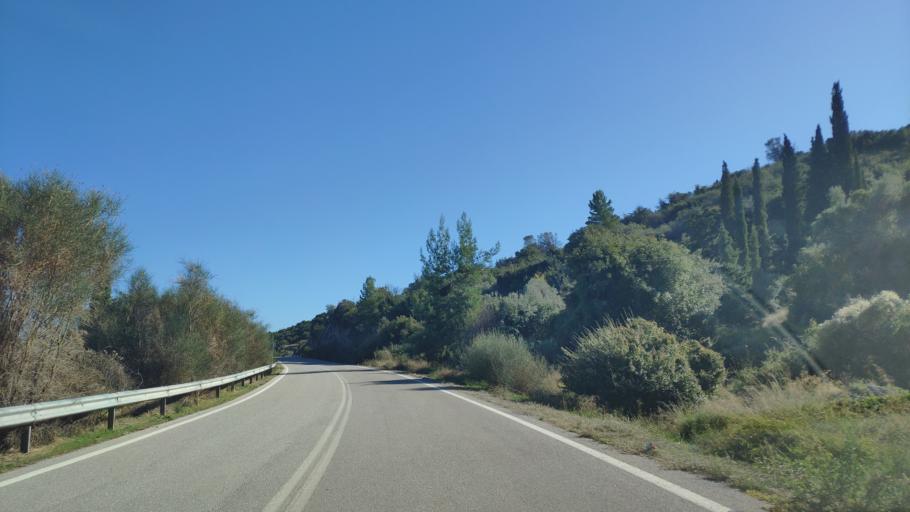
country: GR
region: Peloponnese
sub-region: Nomos Argolidos
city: Palaia Epidavros
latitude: 37.5798
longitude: 23.2358
